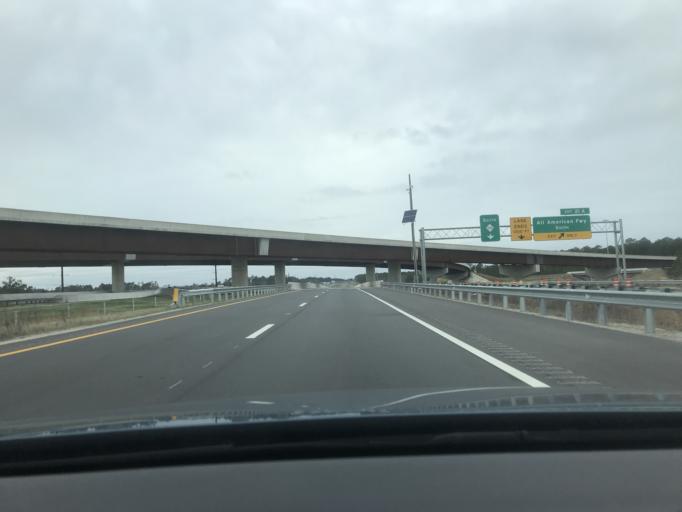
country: US
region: North Carolina
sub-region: Cumberland County
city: Fort Bragg
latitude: 35.1118
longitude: -78.9737
